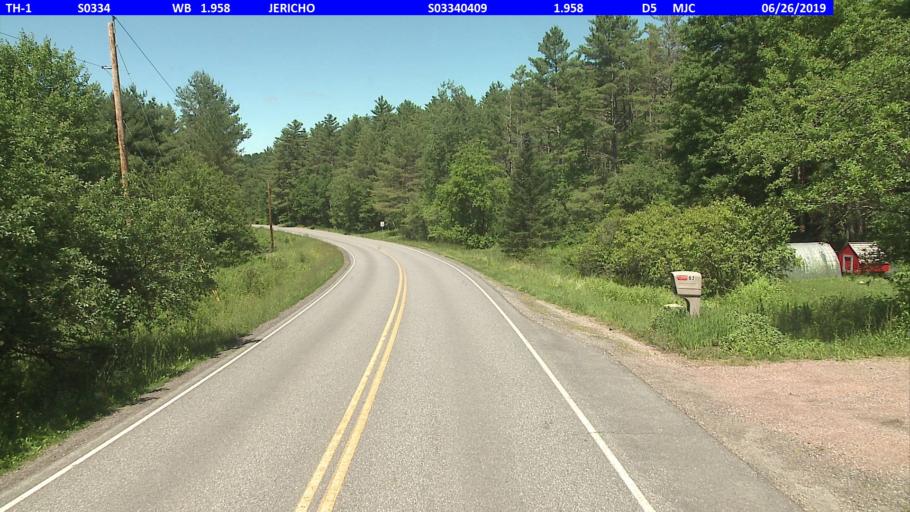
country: US
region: Vermont
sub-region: Chittenden County
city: Jericho
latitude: 44.4627
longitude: -72.9835
